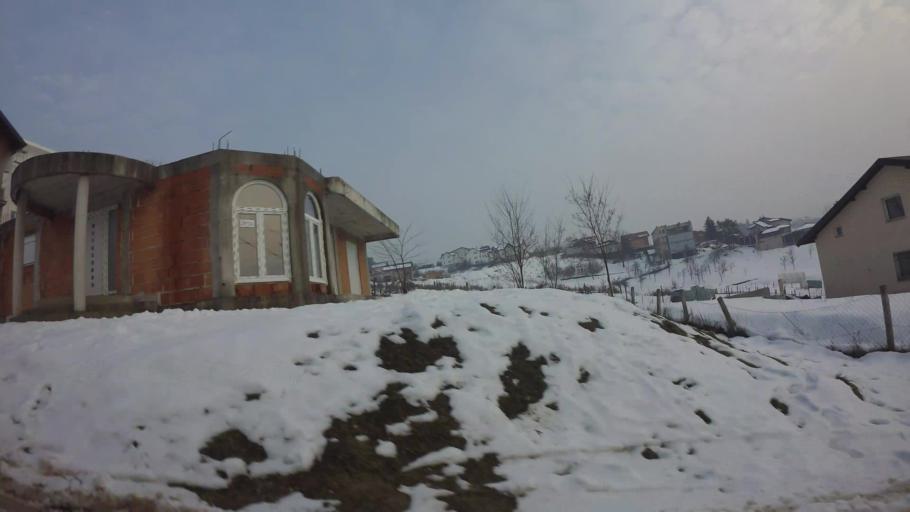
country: BA
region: Federation of Bosnia and Herzegovina
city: Hotonj
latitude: 43.8977
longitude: 18.3792
